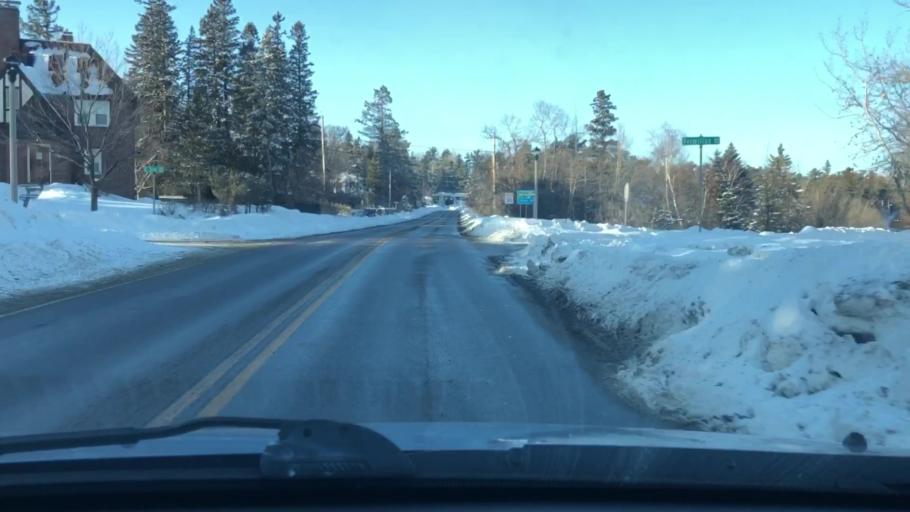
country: US
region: Minnesota
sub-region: Saint Louis County
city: Duluth
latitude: 46.8165
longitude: -92.0689
